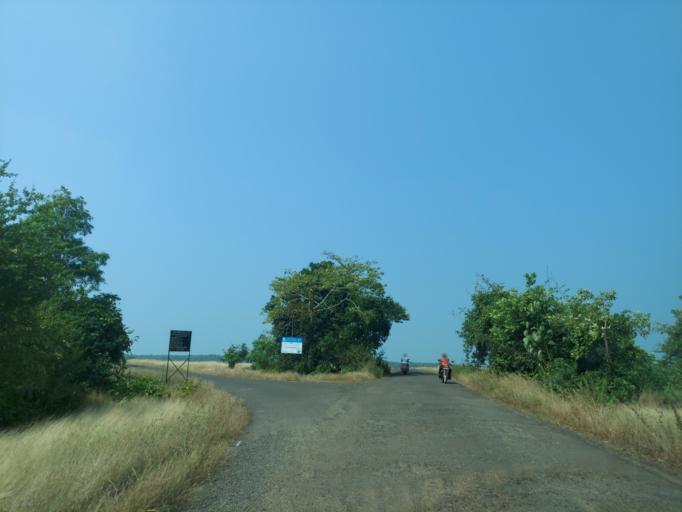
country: IN
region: Maharashtra
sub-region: Sindhudurg
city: Malvan
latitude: 15.9981
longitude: 73.5148
